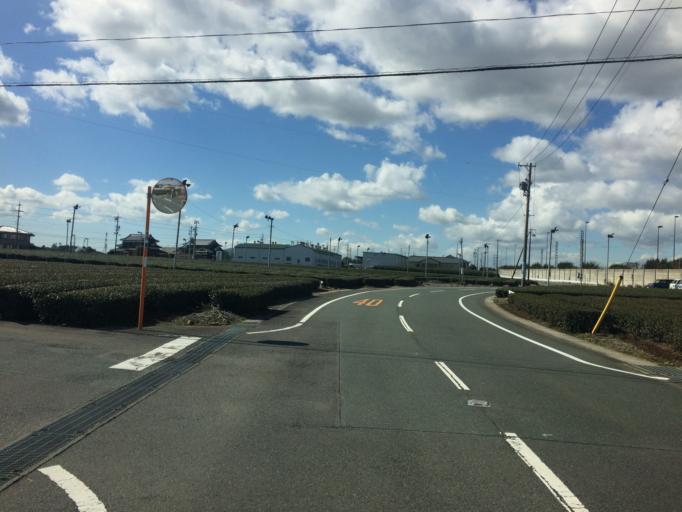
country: JP
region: Shizuoka
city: Shimada
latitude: 34.7588
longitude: 138.1597
